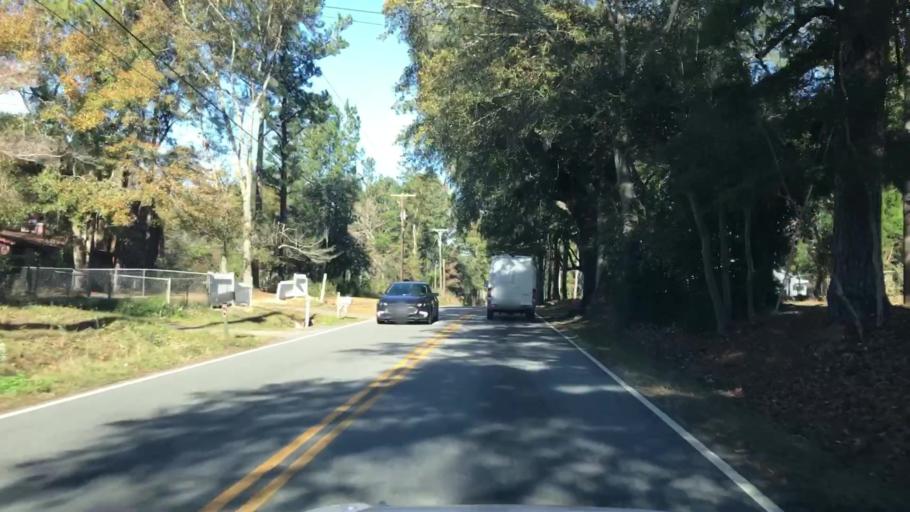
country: US
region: South Carolina
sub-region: Dorchester County
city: Centerville
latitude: 32.9813
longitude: -80.2172
